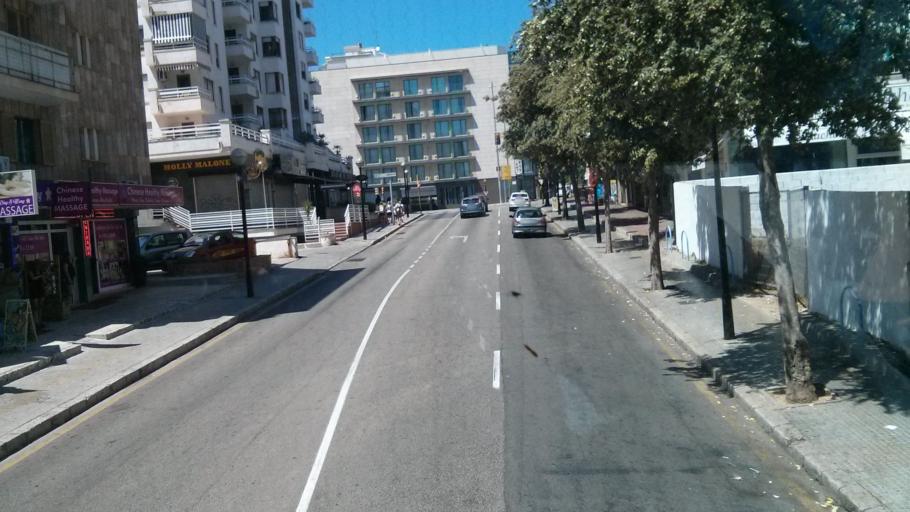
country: ES
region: Balearic Islands
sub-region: Illes Balears
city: Palma
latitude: 39.5695
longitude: 2.6342
